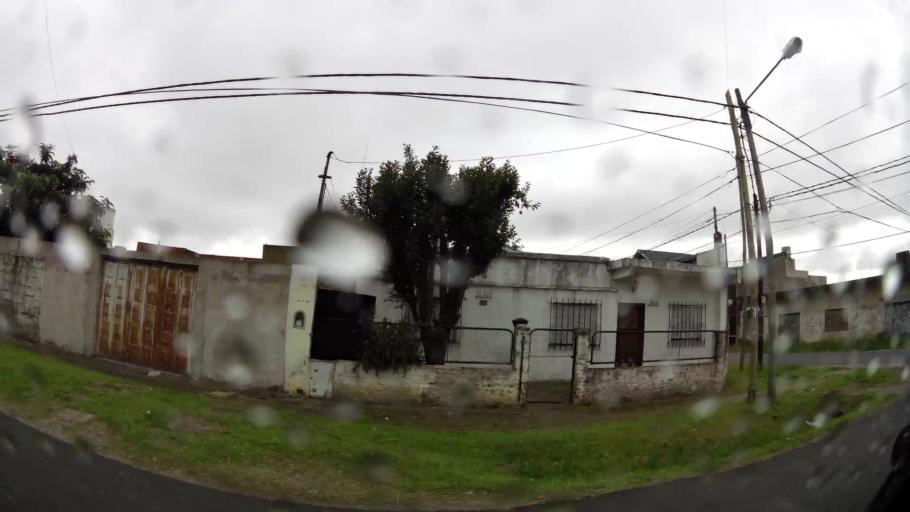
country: AR
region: Buenos Aires
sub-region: Partido de Quilmes
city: Quilmes
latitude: -34.7766
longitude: -58.2350
